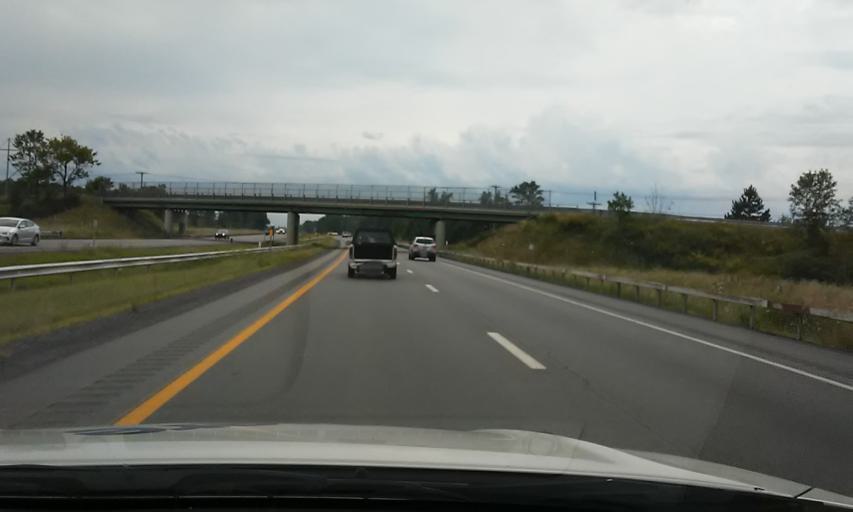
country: US
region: New York
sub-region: Chautauqua County
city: Silver Creek
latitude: 42.4975
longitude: -79.2359
